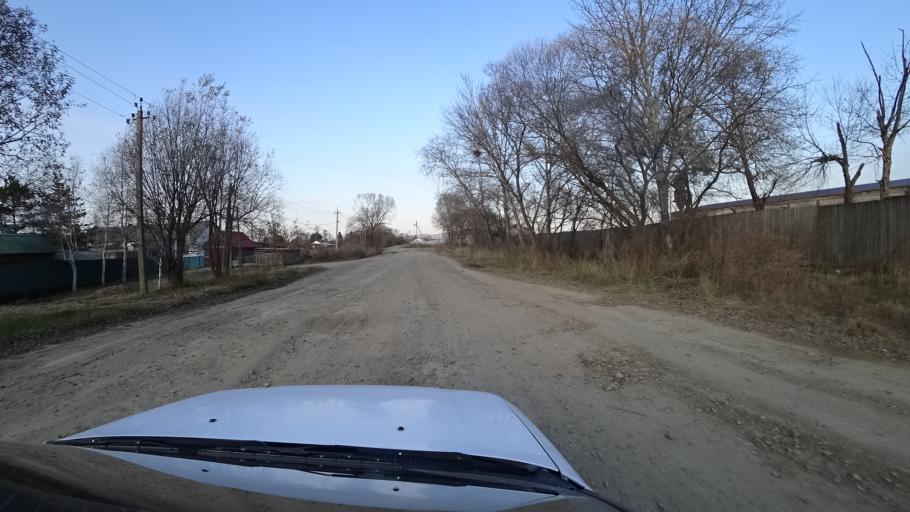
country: RU
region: Primorskiy
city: Dal'nerechensk
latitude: 45.9406
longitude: 133.8216
